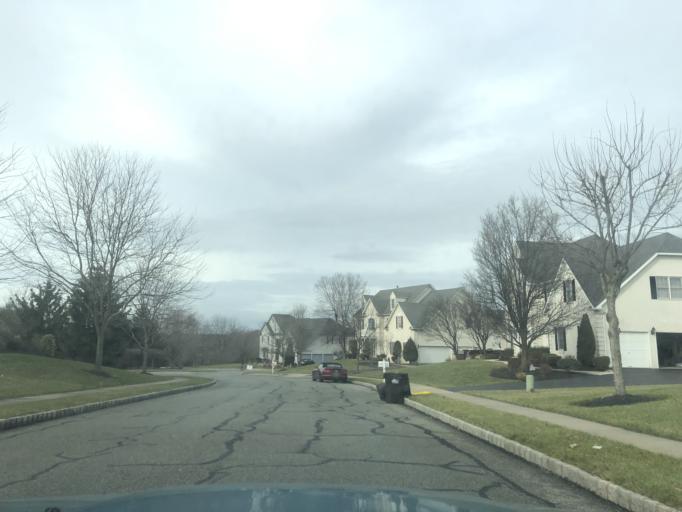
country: US
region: Pennsylvania
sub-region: Montgomery County
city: Harleysville
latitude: 40.2725
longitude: -75.4090
